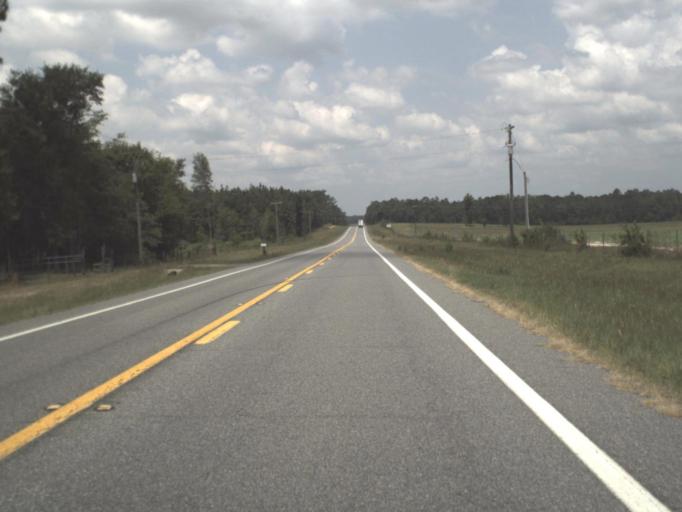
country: US
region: Florida
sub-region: Hamilton County
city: Jasper
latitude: 30.4901
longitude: -83.1369
